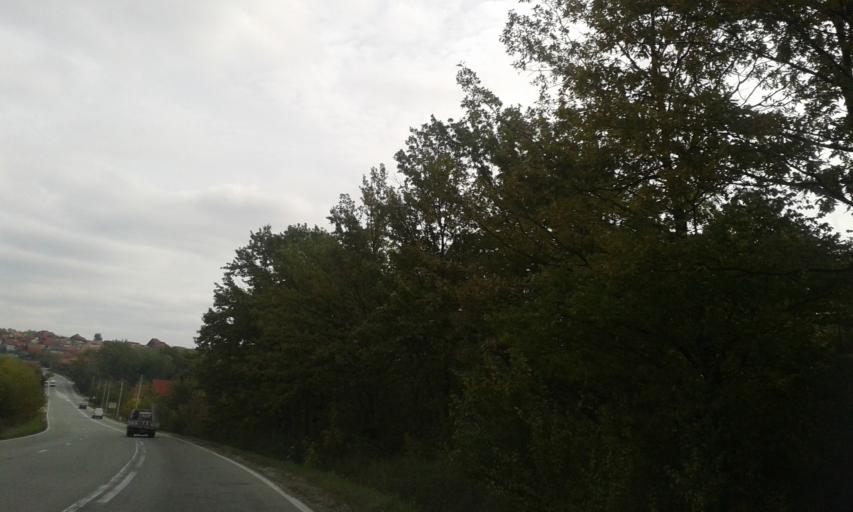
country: RO
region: Gorj
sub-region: Comuna Balanesti
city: Balanesti
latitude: 45.0324
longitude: 23.3893
